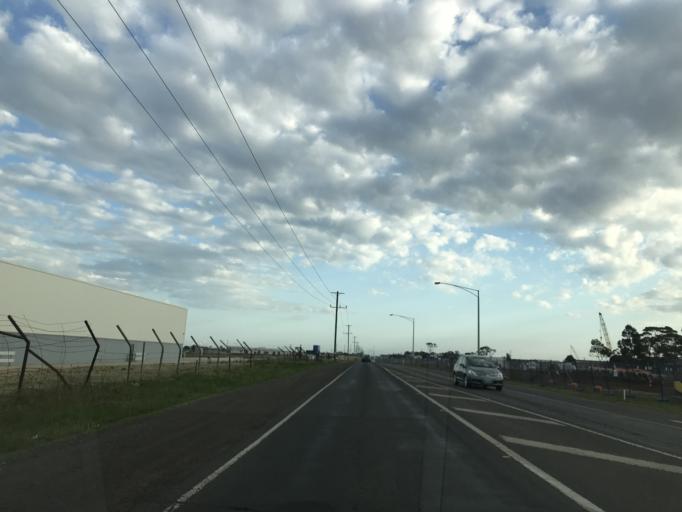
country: AU
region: Victoria
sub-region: Wyndham
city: Truganina
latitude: -37.8187
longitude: 144.7498
